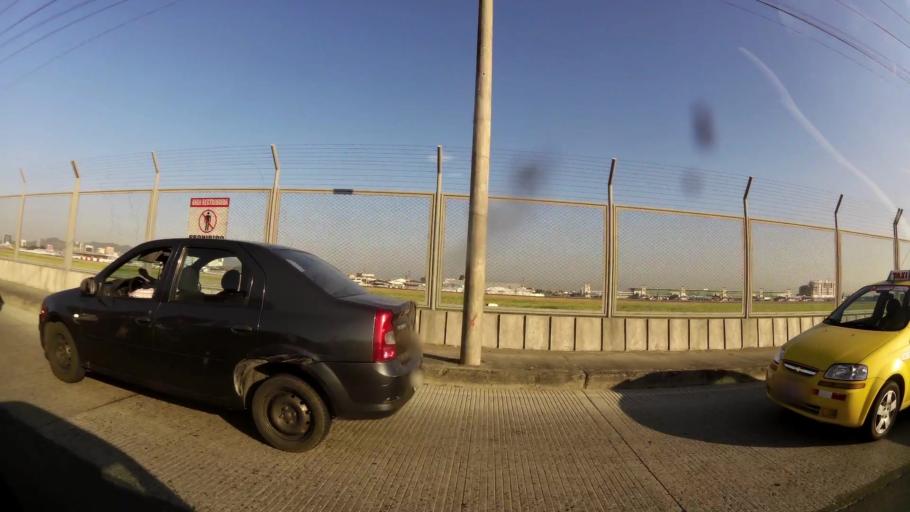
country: EC
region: Guayas
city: Eloy Alfaro
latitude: -2.1552
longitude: -79.8803
